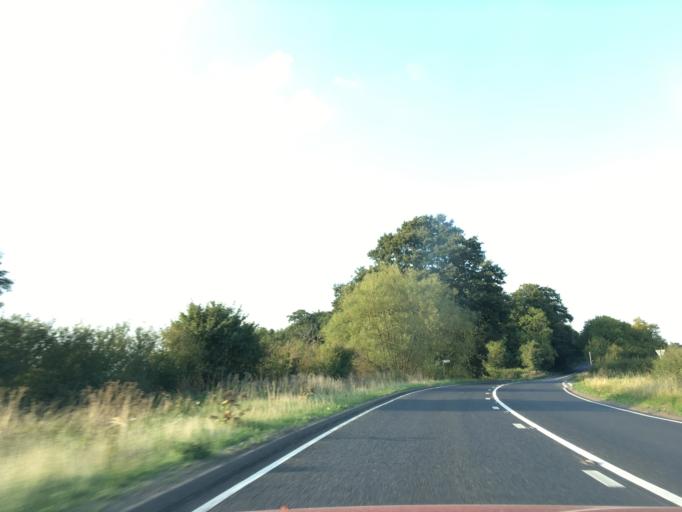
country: GB
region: England
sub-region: Gloucestershire
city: Moreton in Marsh
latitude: 52.0043
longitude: -1.6967
